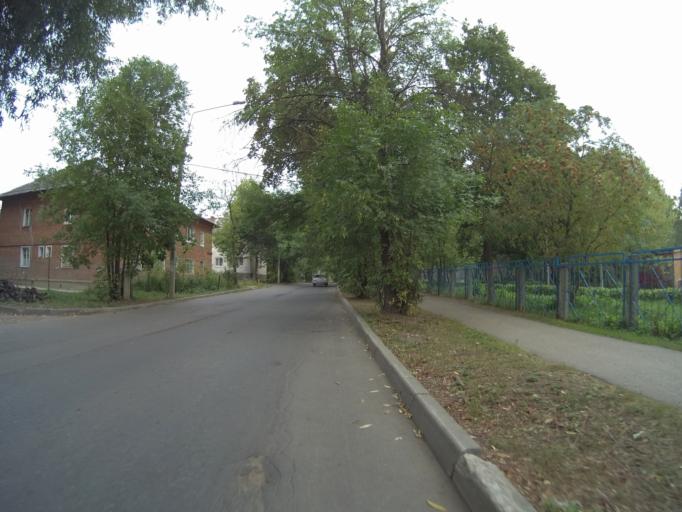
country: RU
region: Vladimir
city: Vladimir
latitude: 56.1242
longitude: 40.3539
